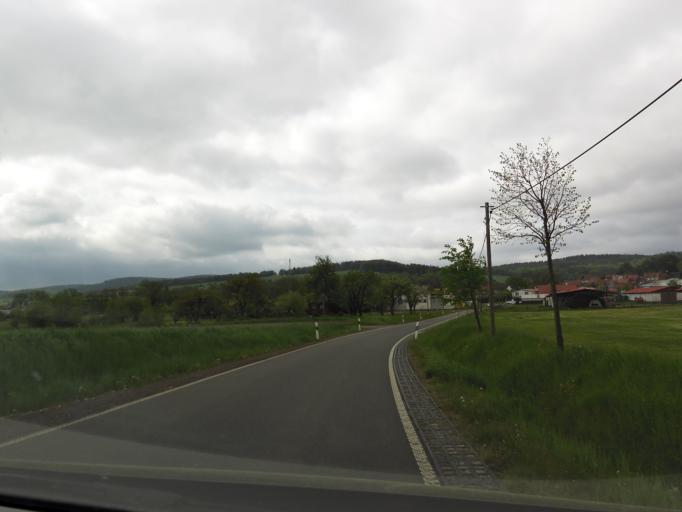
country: DE
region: Thuringia
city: Ernstroda
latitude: 50.8698
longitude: 10.6220
